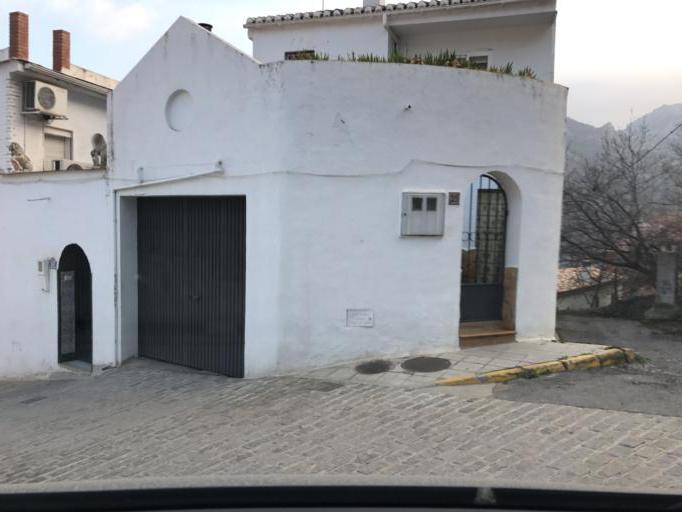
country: ES
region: Andalusia
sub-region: Provincia de Granada
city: Guejar-Sierra
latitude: 37.1616
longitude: -3.4431
